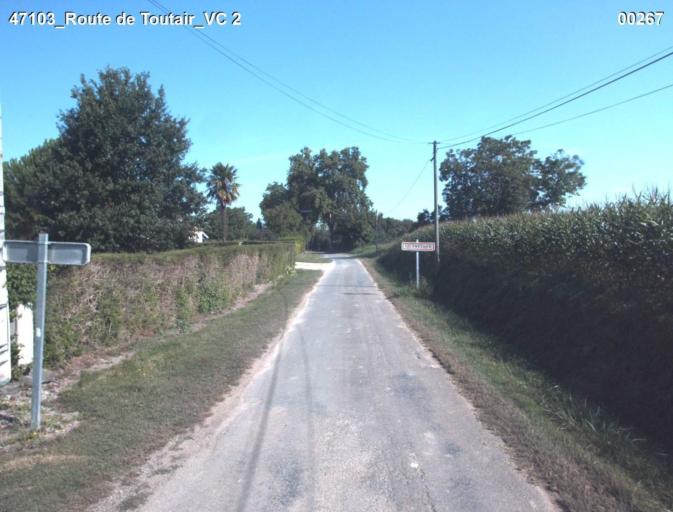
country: FR
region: Aquitaine
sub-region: Departement du Lot-et-Garonne
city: Nerac
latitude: 44.0829
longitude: 0.3220
